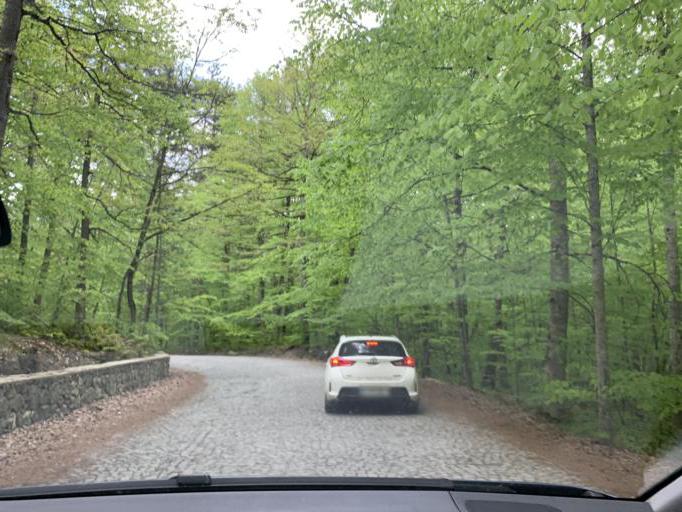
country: TR
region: Zonguldak
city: Egerci
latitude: 40.9394
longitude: 31.7436
